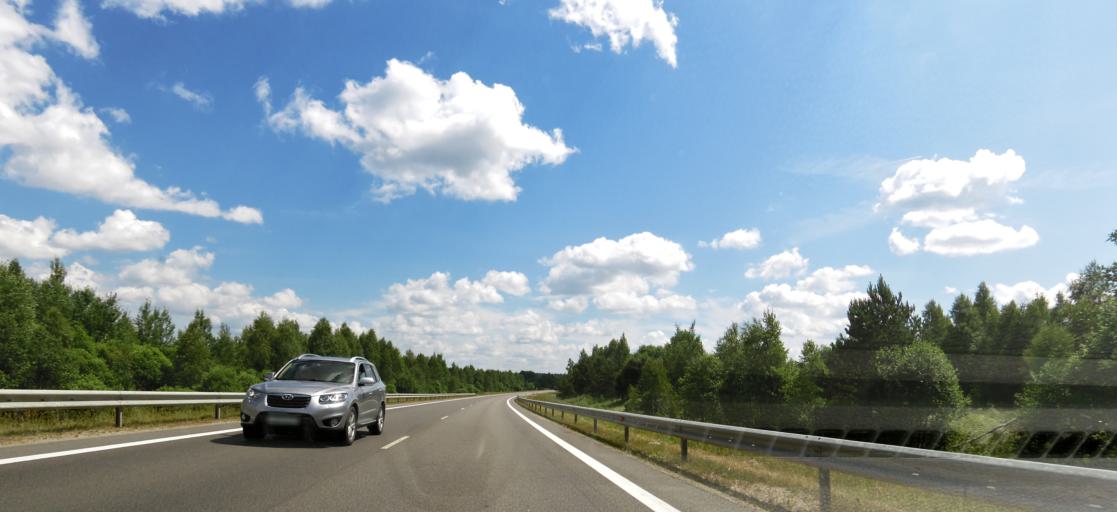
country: LT
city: Skaidiskes
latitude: 54.5612
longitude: 25.6565
